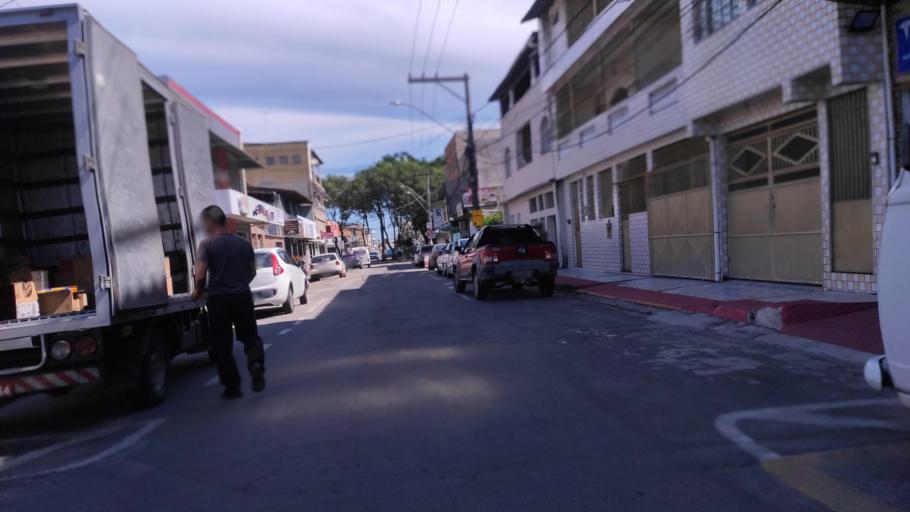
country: BR
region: Espirito Santo
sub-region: Serra
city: Serra
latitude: -20.1944
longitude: -40.2703
